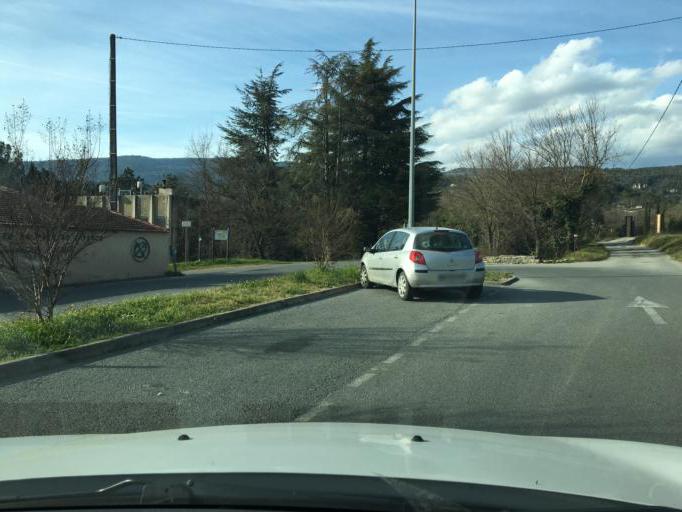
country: FR
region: Provence-Alpes-Cote d'Azur
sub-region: Departement du Var
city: Fayence
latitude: 43.6252
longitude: 6.6883
